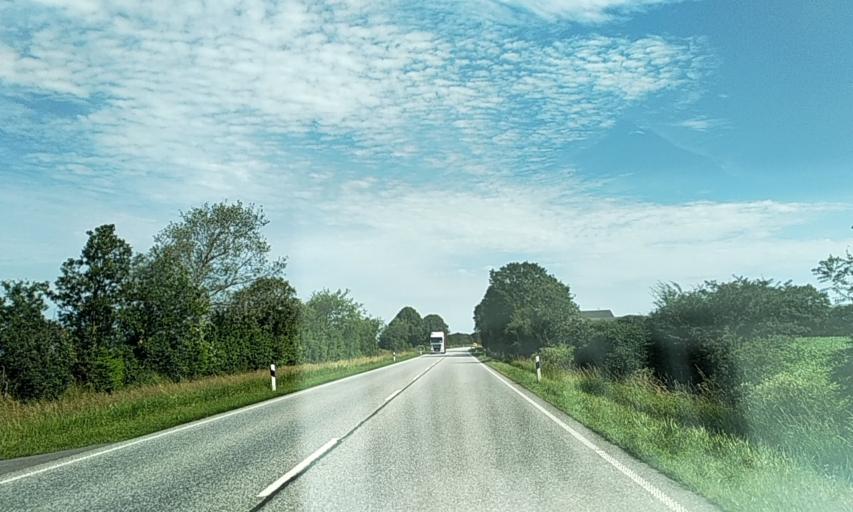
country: DE
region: Schleswig-Holstein
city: Jagel
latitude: 54.4369
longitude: 9.5334
